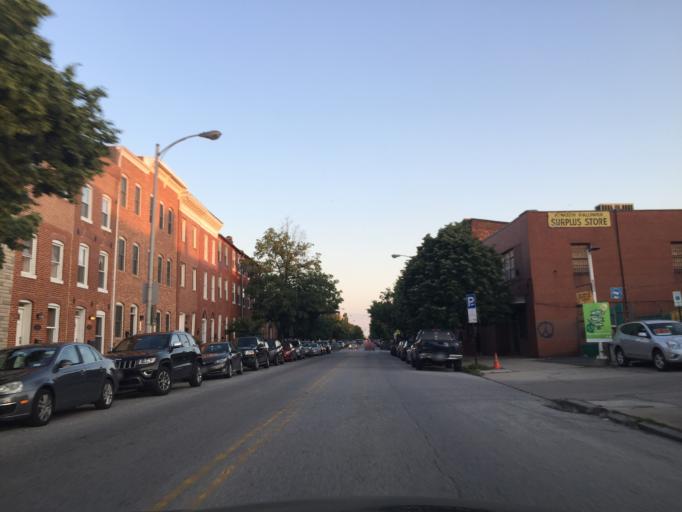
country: US
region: Maryland
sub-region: City of Baltimore
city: Baltimore
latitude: 39.2766
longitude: -76.6155
